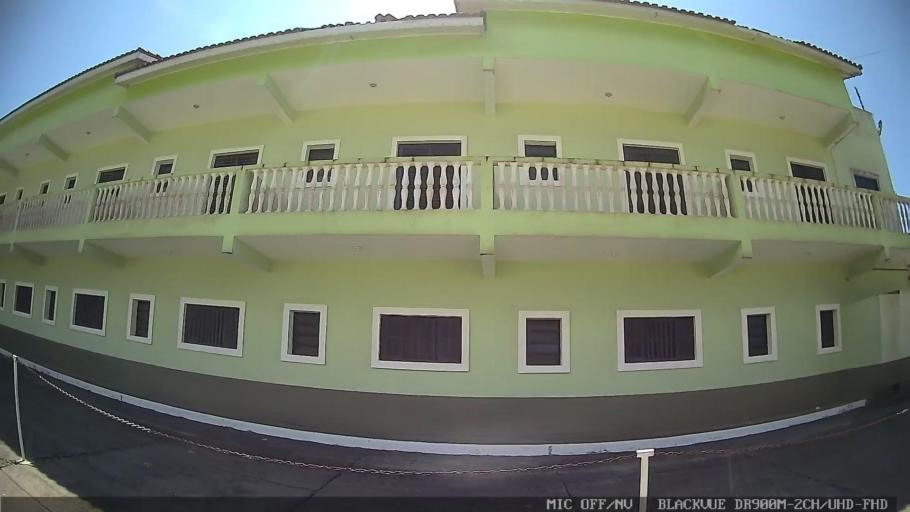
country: BR
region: Sao Paulo
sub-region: Peruibe
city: Peruibe
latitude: -24.3334
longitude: -47.0026
